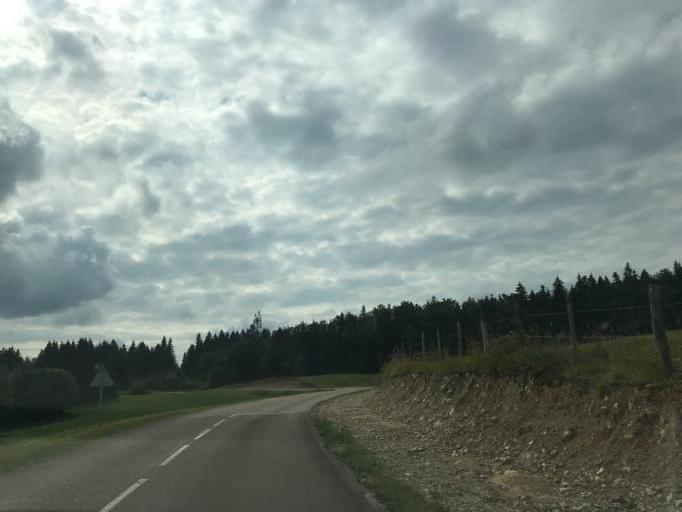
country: FR
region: Franche-Comte
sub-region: Departement du Jura
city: Longchaumois
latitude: 46.5062
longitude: 5.8943
